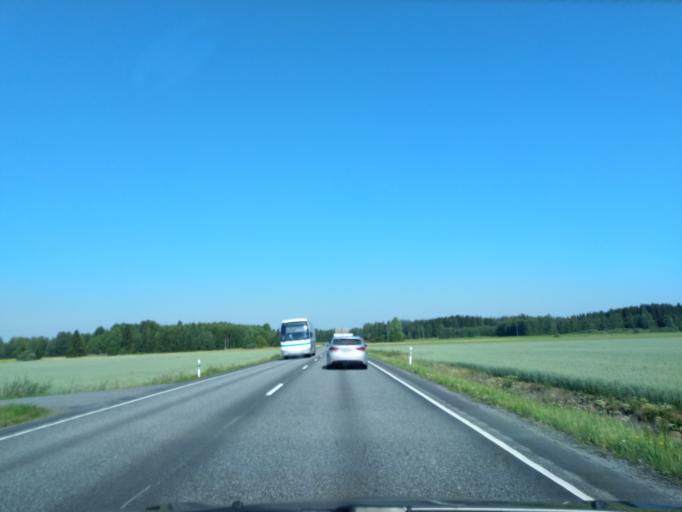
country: FI
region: Varsinais-Suomi
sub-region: Loimaa
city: Alastaro
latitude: 61.0951
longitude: 22.8723
